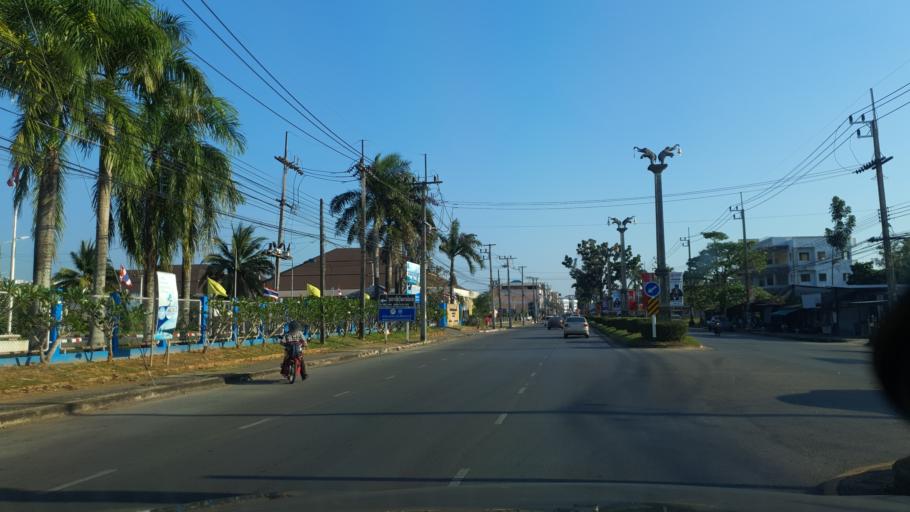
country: TH
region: Krabi
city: Krabi
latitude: 8.0718
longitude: 98.9120
